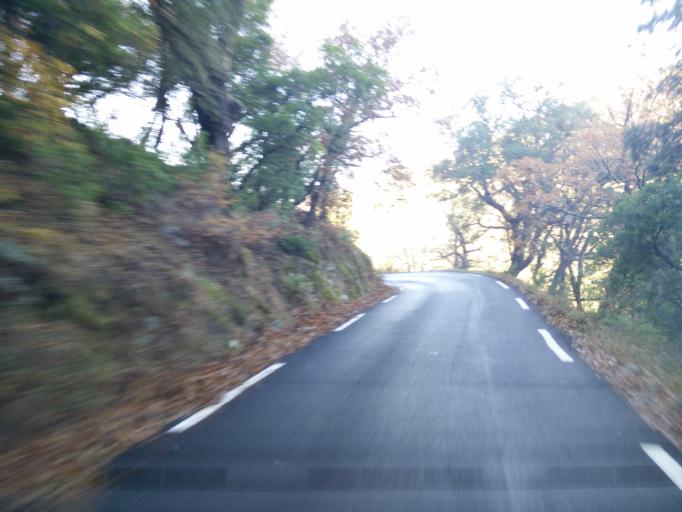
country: FR
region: Provence-Alpes-Cote d'Azur
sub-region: Departement du Var
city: Collobrieres
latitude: 43.2396
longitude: 6.3476
